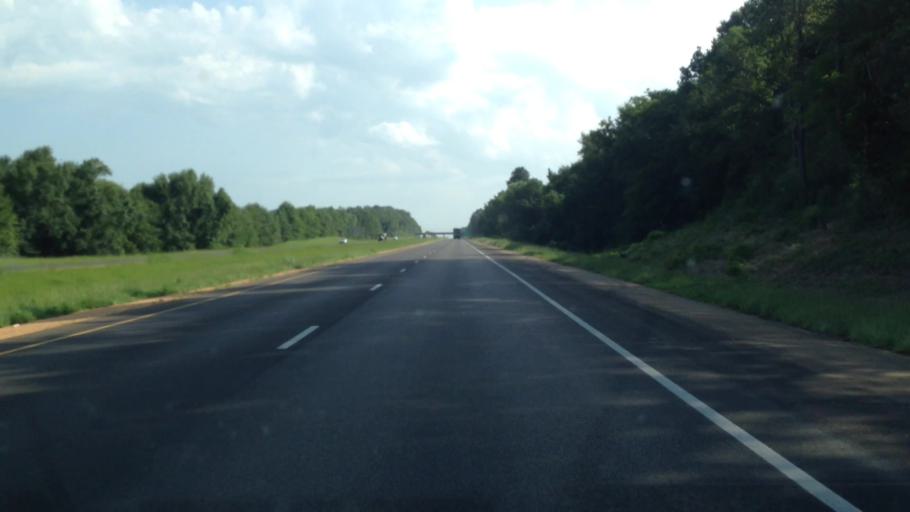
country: US
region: Mississippi
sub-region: Copiah County
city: Crystal Springs
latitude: 31.9845
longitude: -90.3744
